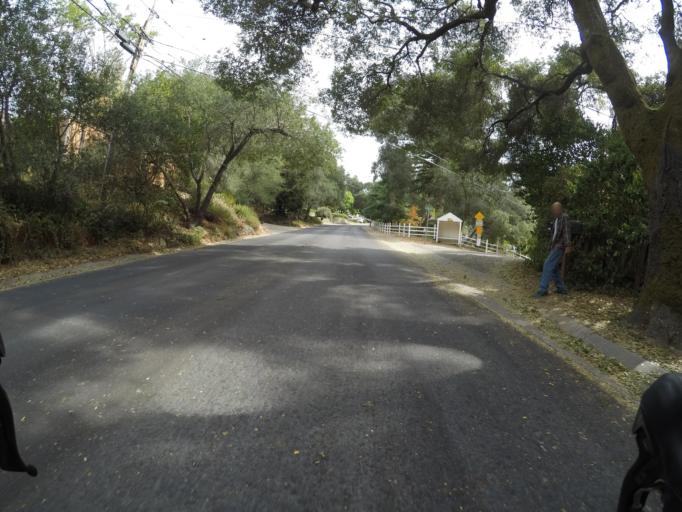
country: US
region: California
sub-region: Santa Cruz County
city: Ben Lomond
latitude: 37.0733
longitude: -122.0745
